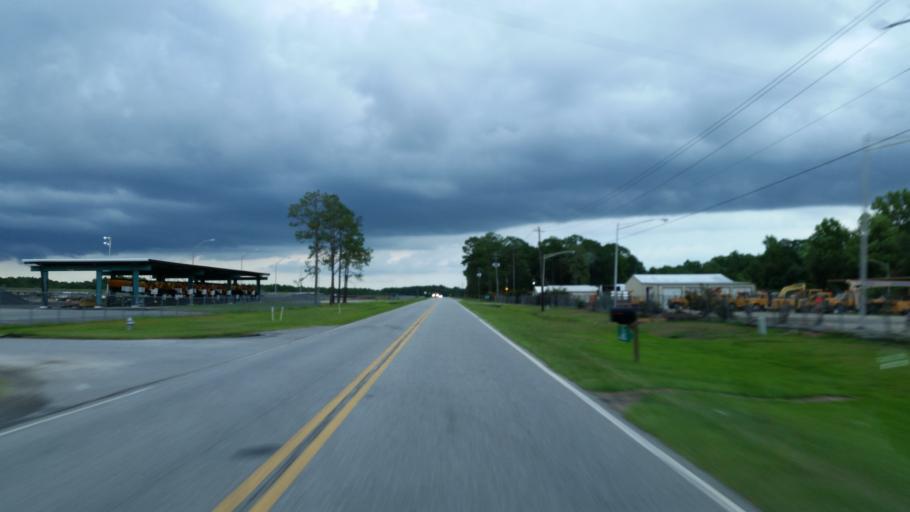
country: US
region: Georgia
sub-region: Tift County
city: Unionville
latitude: 31.4221
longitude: -83.4911
